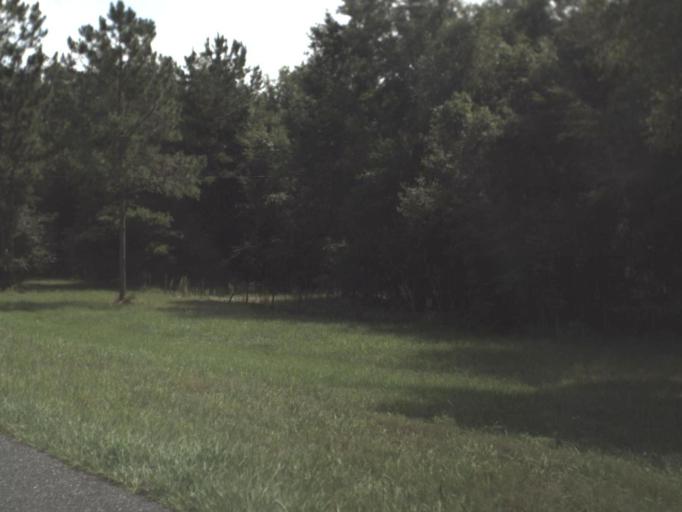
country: US
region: Florida
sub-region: Alachua County
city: High Springs
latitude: 29.8641
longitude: -82.6087
